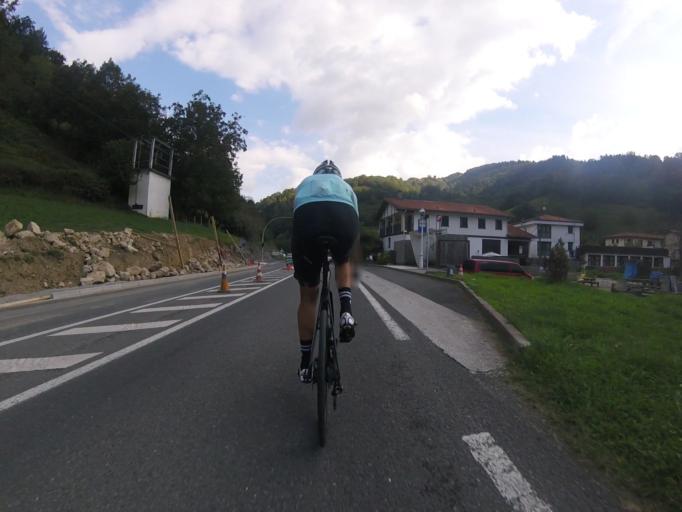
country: ES
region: Basque Country
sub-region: Provincia de Guipuzcoa
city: Amezqueta
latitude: 43.0679
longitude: -2.0847
